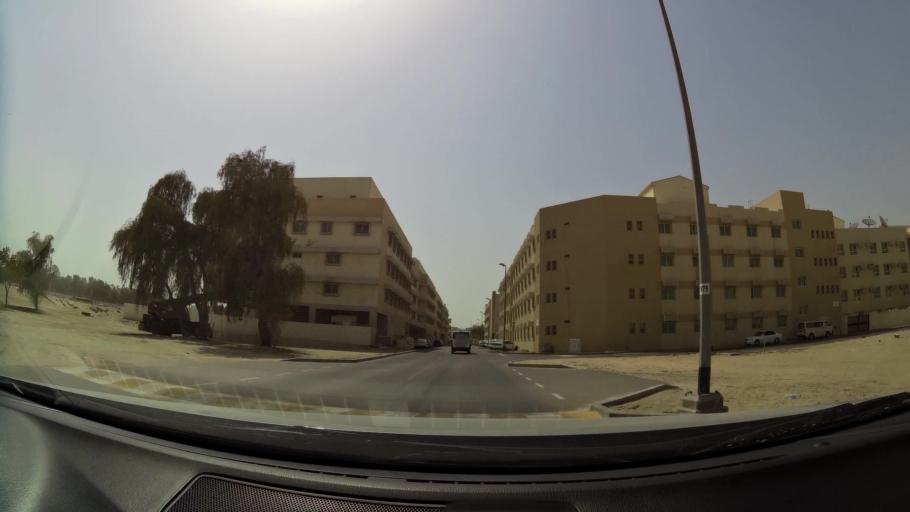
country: AE
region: Dubai
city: Dubai
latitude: 25.1475
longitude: 55.2501
